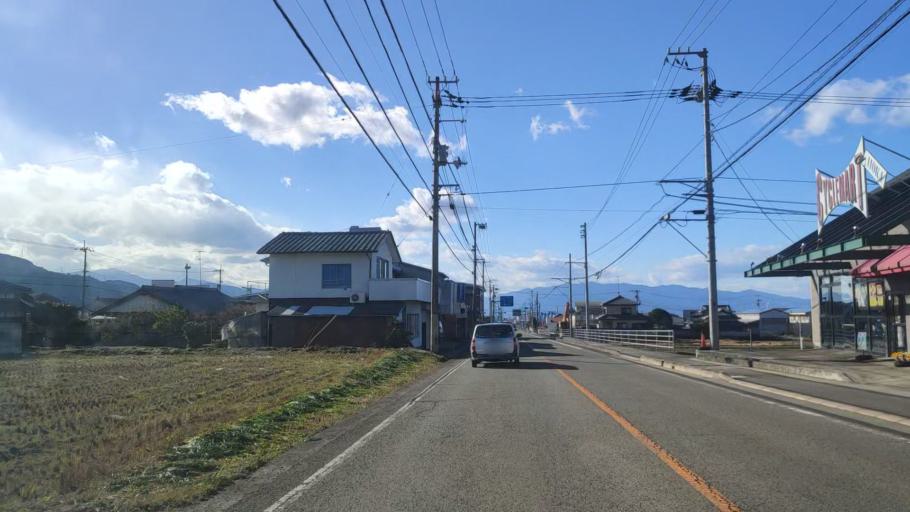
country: JP
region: Ehime
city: Saijo
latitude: 33.9186
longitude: 133.2266
